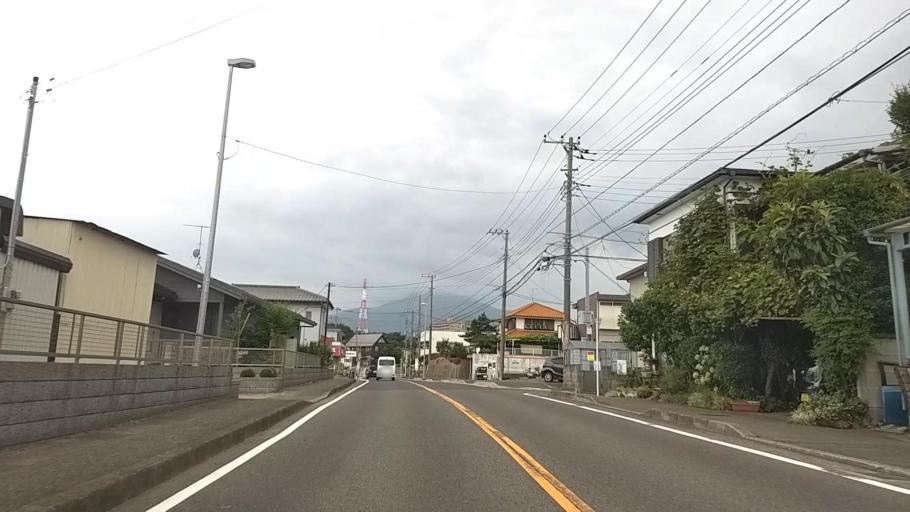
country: JP
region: Kanagawa
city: Isehara
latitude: 35.3882
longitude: 139.3285
